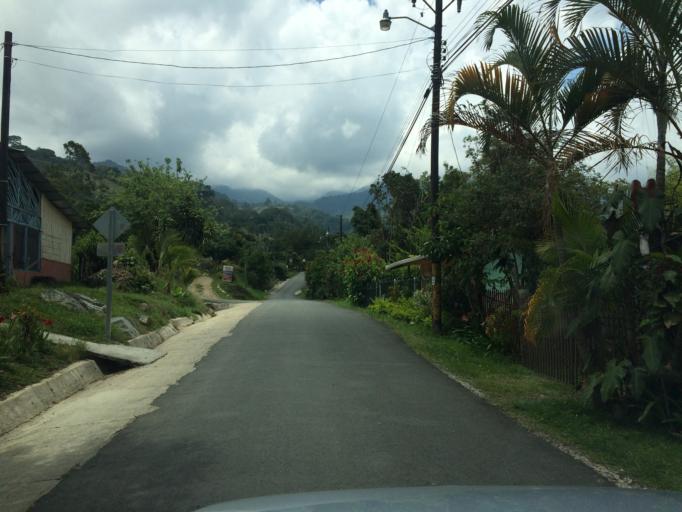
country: CR
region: San Jose
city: San Isidro
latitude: 9.4538
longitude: -83.6074
